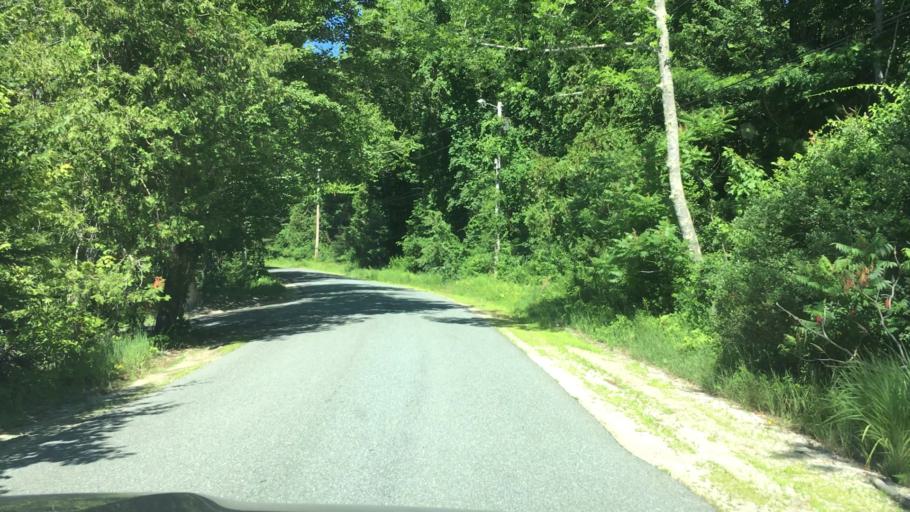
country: US
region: Maine
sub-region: Hancock County
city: Sedgwick
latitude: 44.3172
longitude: -68.6119
